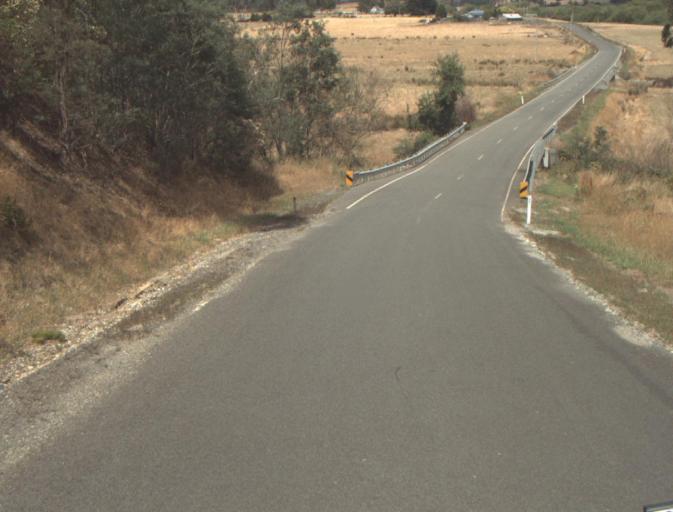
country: AU
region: Tasmania
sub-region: Launceston
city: Mayfield
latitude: -41.2190
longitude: 147.1376
